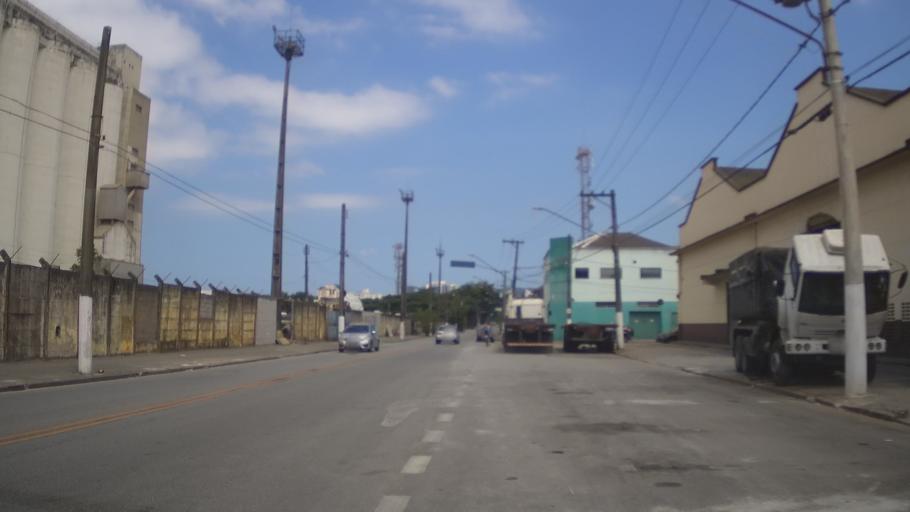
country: BR
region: Sao Paulo
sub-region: Santos
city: Santos
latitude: -23.9584
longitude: -46.3089
